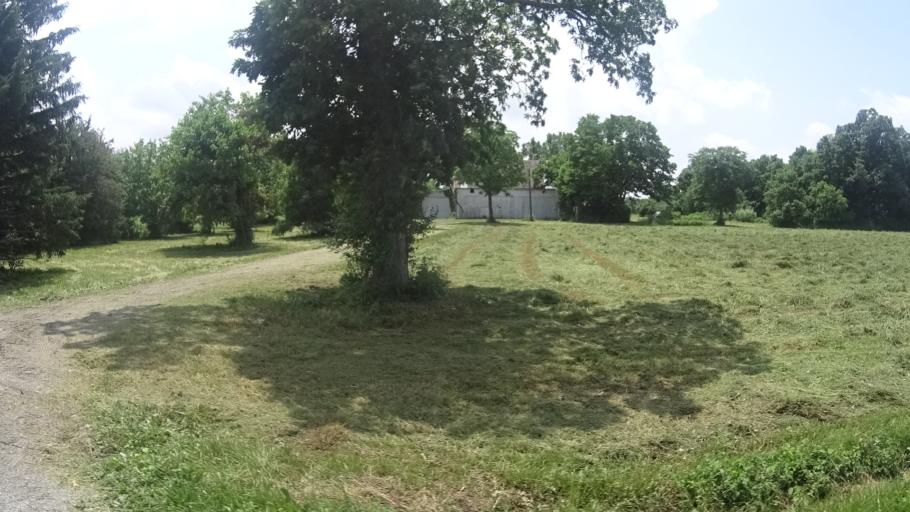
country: US
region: Ohio
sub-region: Huron County
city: Bellevue
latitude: 41.3251
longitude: -82.7795
